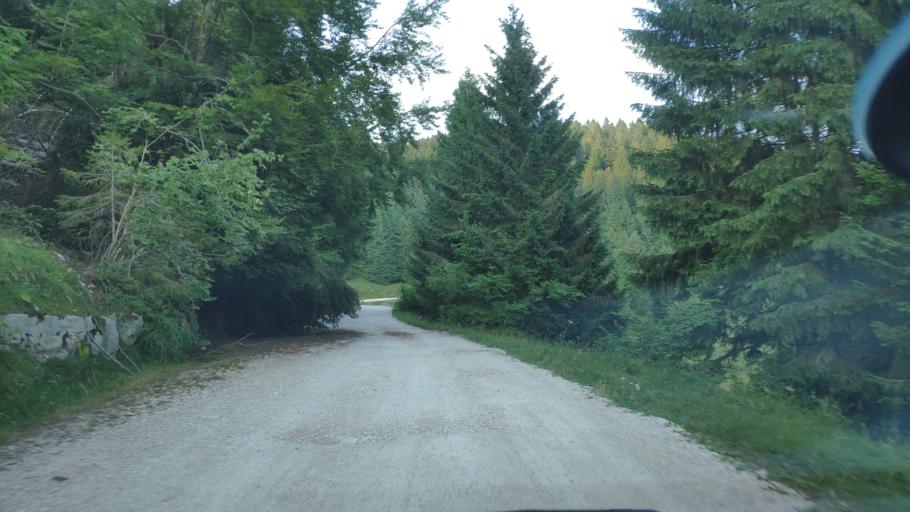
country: IT
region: Veneto
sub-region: Provincia di Vicenza
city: Calvene
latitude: 45.8018
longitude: 11.5085
